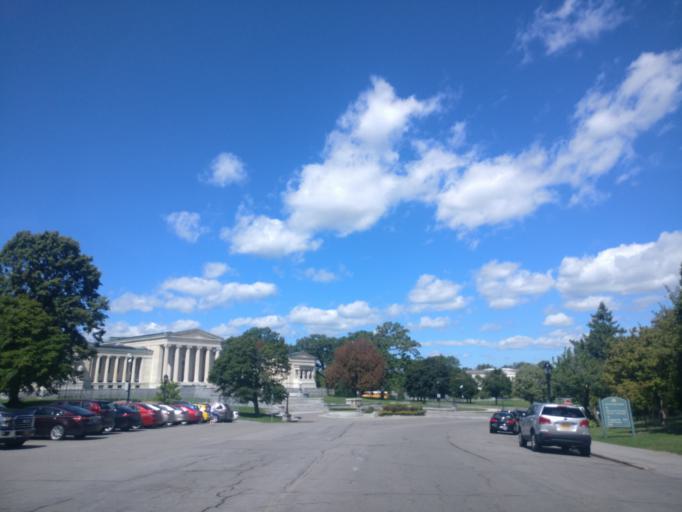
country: US
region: New York
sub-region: Erie County
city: Kenmore
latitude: 42.9318
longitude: -78.8741
